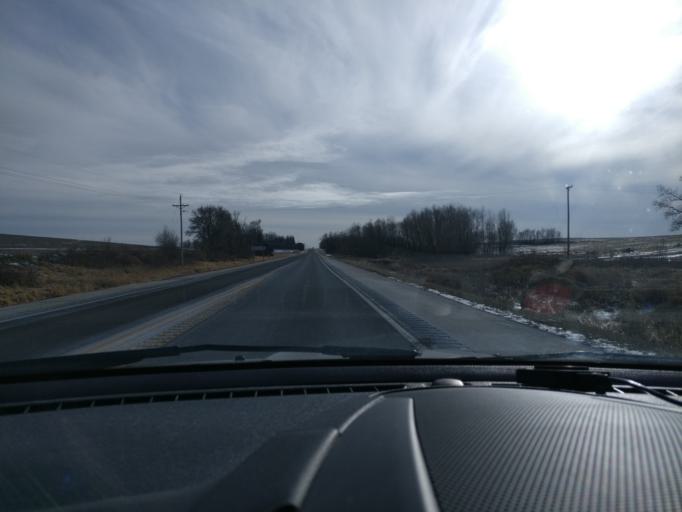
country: US
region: Nebraska
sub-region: Dodge County
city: Fremont
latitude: 41.3757
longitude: -96.5020
